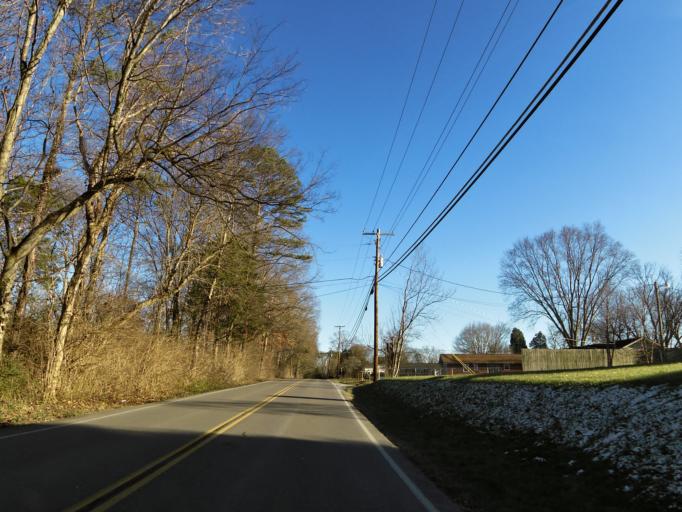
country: US
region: Tennessee
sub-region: Knox County
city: Farragut
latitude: 35.9496
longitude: -84.0604
